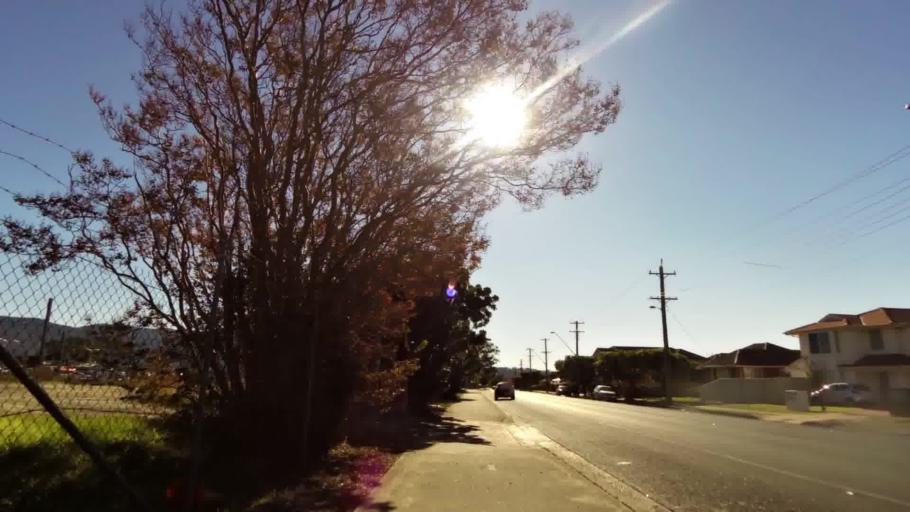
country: AU
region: New South Wales
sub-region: Wollongong
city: Dapto
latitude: -34.4916
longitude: 150.7934
